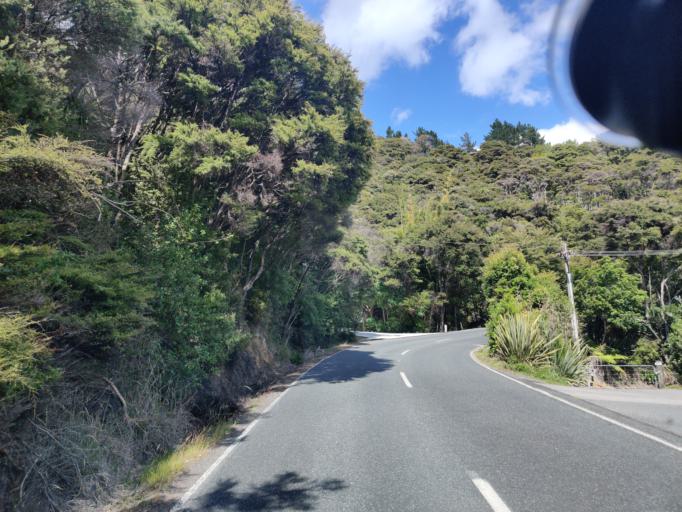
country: NZ
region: Northland
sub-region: Far North District
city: Paihia
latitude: -35.2577
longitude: 174.2400
